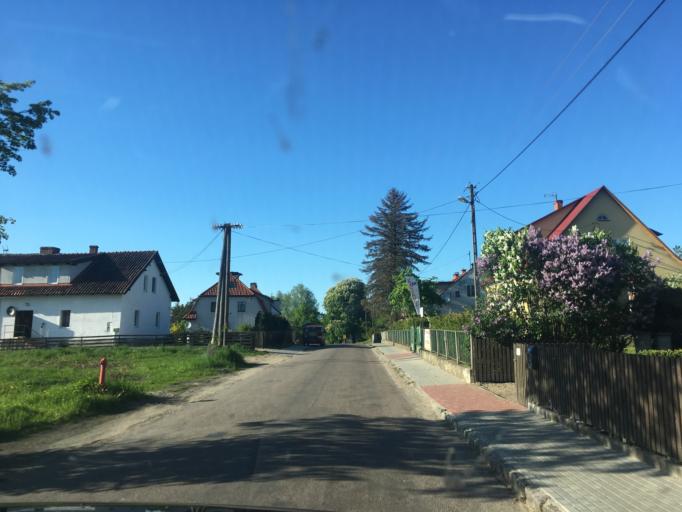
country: PL
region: Warmian-Masurian Voivodeship
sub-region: Powiat piski
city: Ruciane-Nida
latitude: 53.6850
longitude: 21.4997
